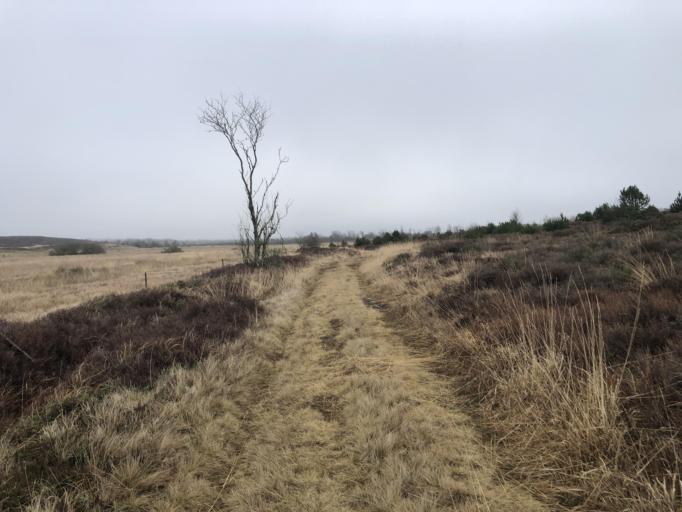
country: DK
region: Central Jutland
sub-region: Holstebro Kommune
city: Holstebro
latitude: 56.2509
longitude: 8.5148
